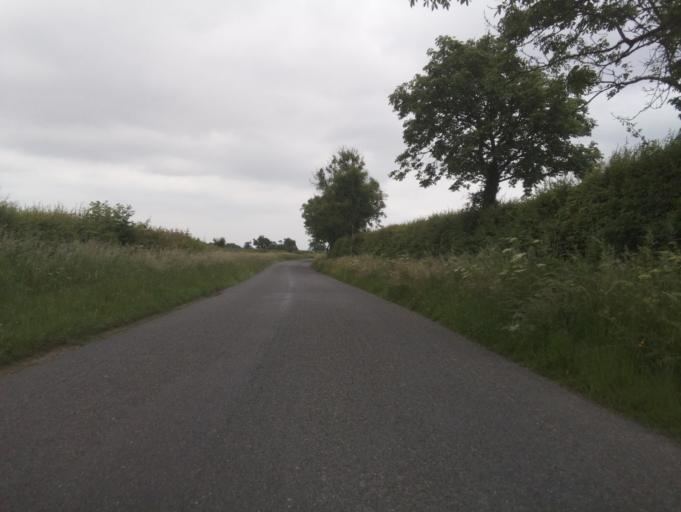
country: GB
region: England
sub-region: District of Rutland
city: Langham
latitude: 52.6706
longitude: -0.7647
